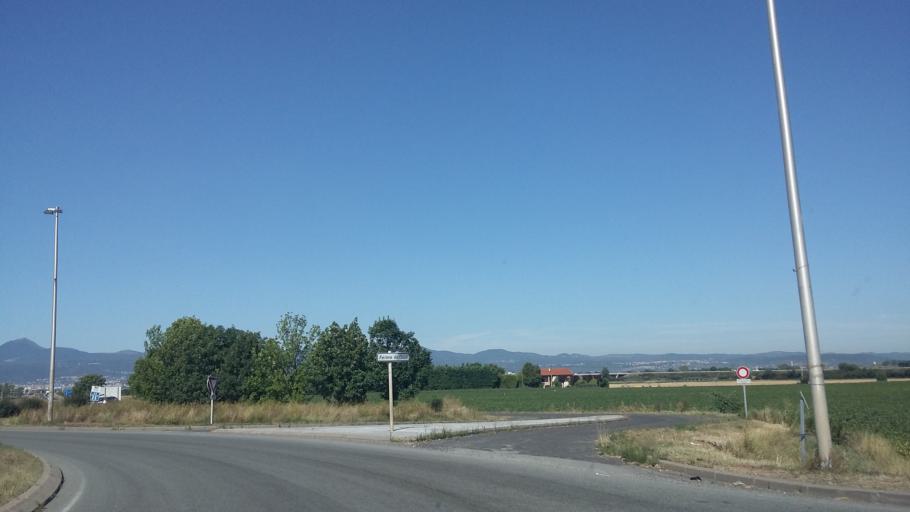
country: FR
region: Auvergne
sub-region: Departement du Puy-de-Dome
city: Dallet
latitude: 45.7849
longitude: 3.2140
